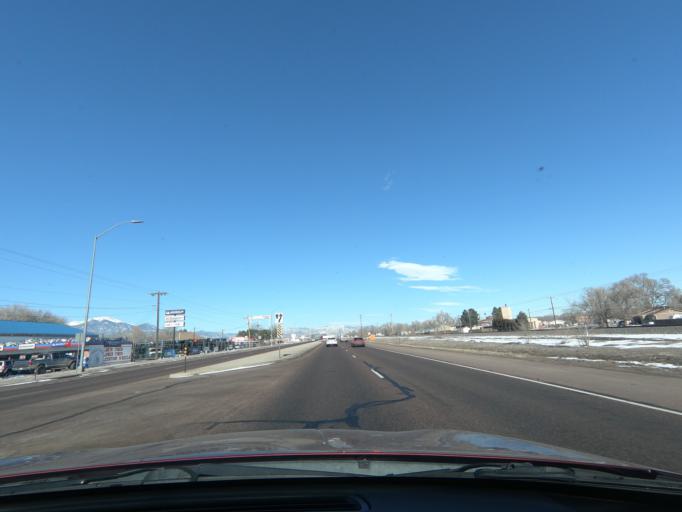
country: US
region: Colorado
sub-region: El Paso County
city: Security-Widefield
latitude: 38.7480
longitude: -104.7411
